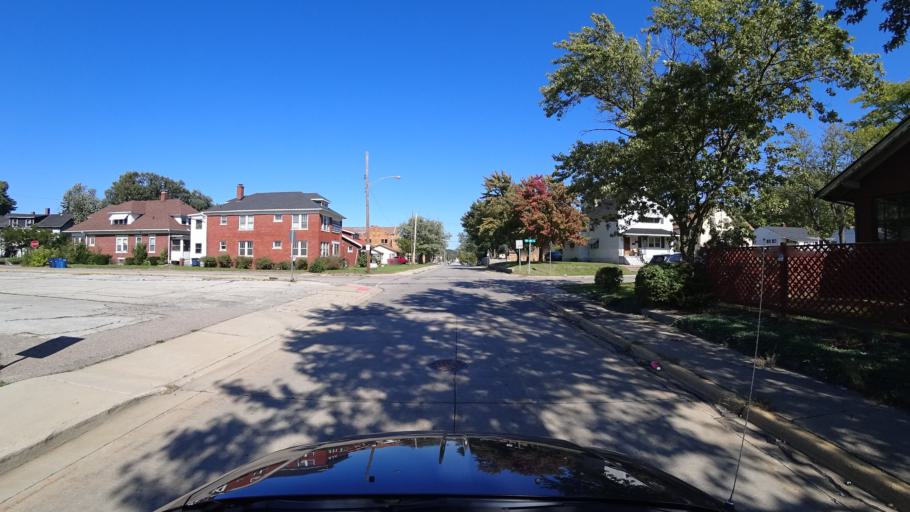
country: US
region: Indiana
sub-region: LaPorte County
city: Michigan City
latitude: 41.7112
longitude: -86.8937
